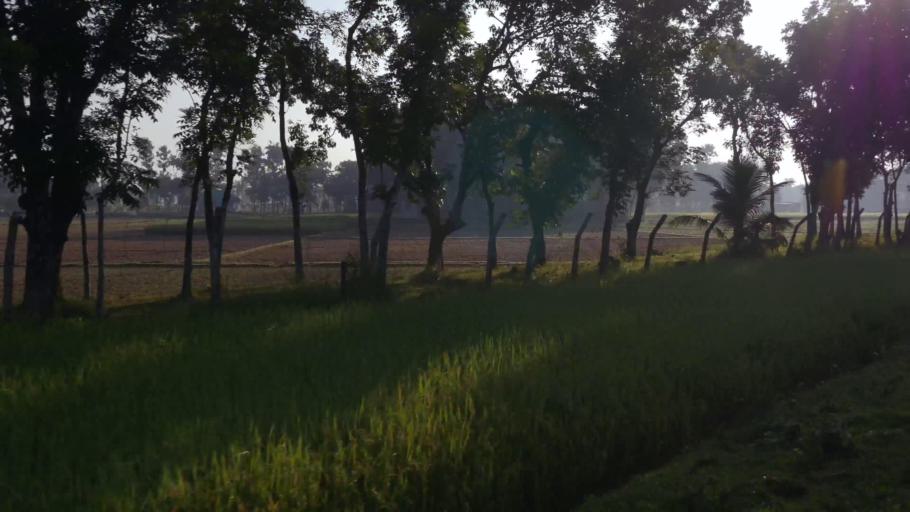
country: BD
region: Dhaka
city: Jamalpur
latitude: 24.9121
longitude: 89.9600
